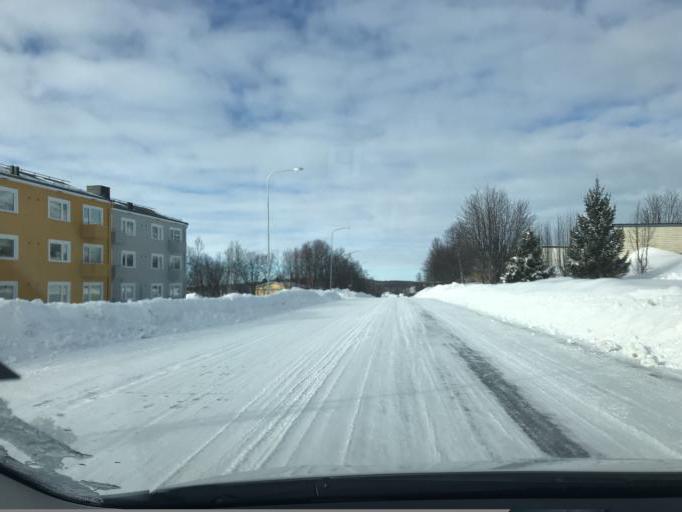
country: SE
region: Norrbotten
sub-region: Kiruna Kommun
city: Kiruna
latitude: 67.8639
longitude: 20.2094
